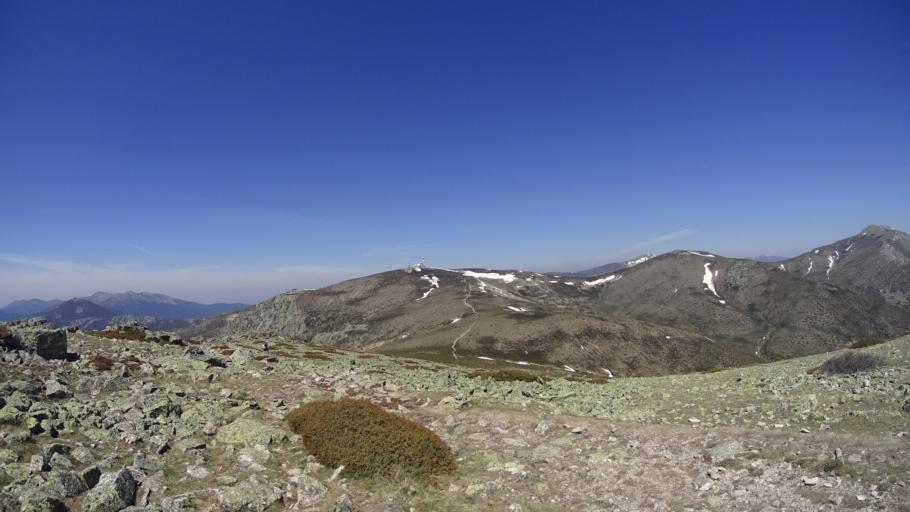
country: ES
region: Madrid
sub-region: Provincia de Madrid
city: Becerril de la Sierra
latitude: 40.7680
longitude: -3.9691
